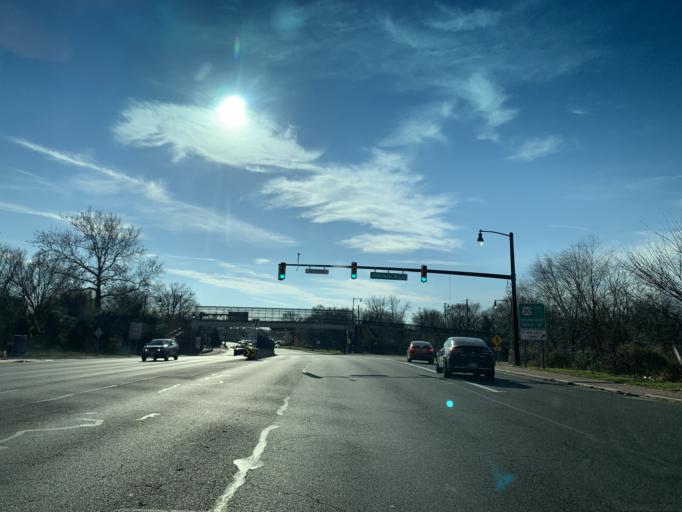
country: US
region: New Jersey
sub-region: Camden County
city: Wood-Lynne
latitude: 39.9190
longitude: -75.0886
